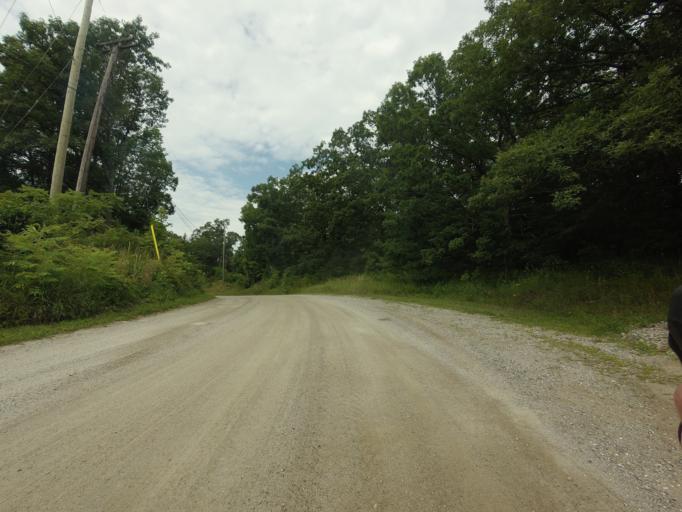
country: CA
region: Ontario
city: Perth
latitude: 44.7335
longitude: -76.6060
